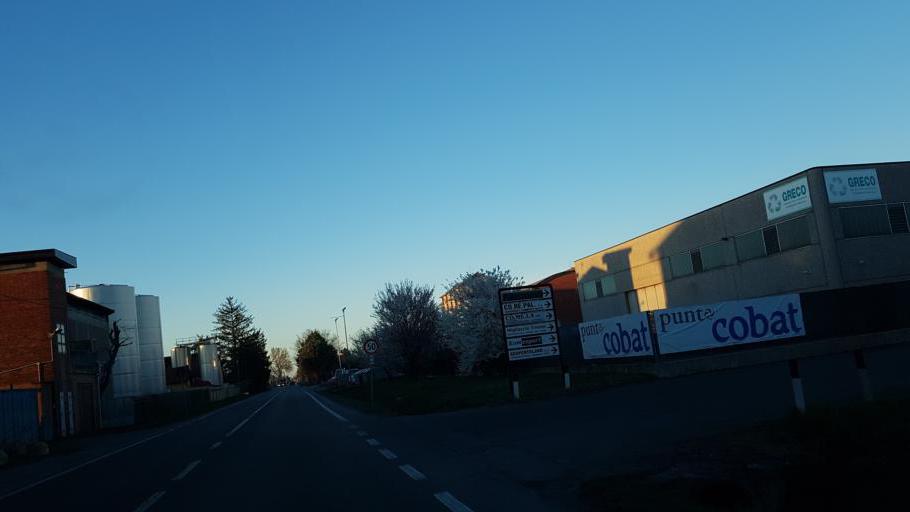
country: IT
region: Piedmont
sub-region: Provincia di Alessandria
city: Carbonara Scrivia
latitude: 44.8588
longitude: 8.8550
